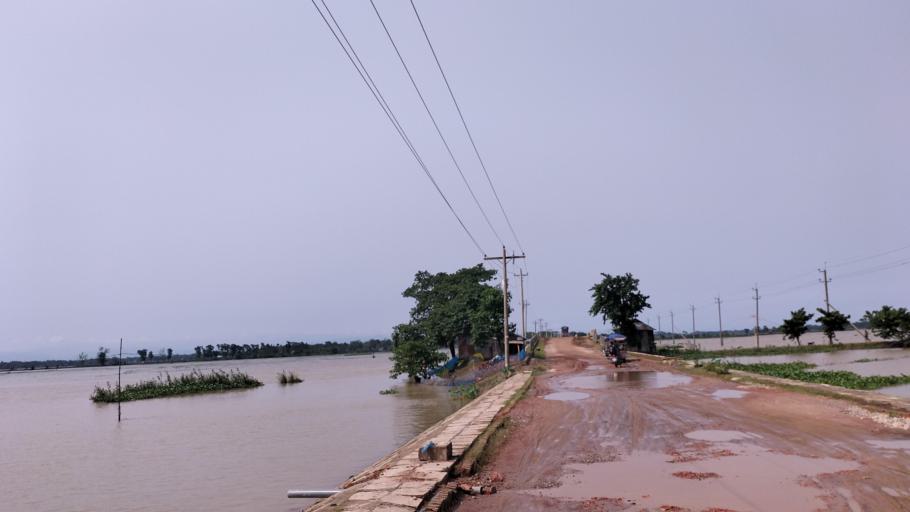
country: BD
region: Dhaka
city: Netrakona
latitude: 25.0193
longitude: 90.8576
